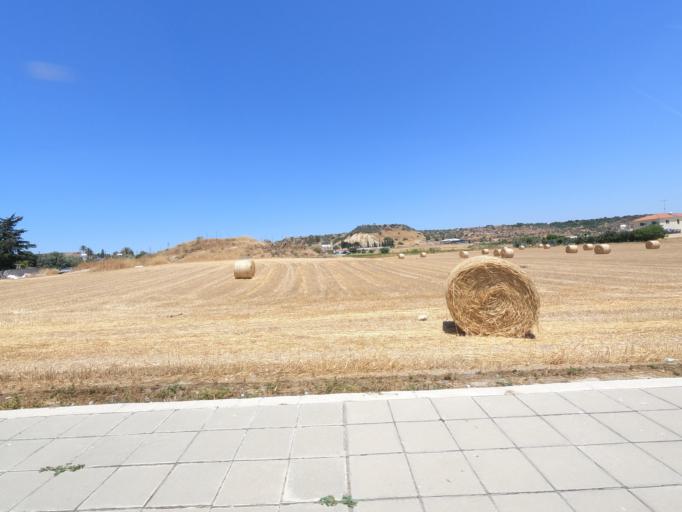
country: CY
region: Larnaka
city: Pyla
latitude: 35.0102
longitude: 33.6940
